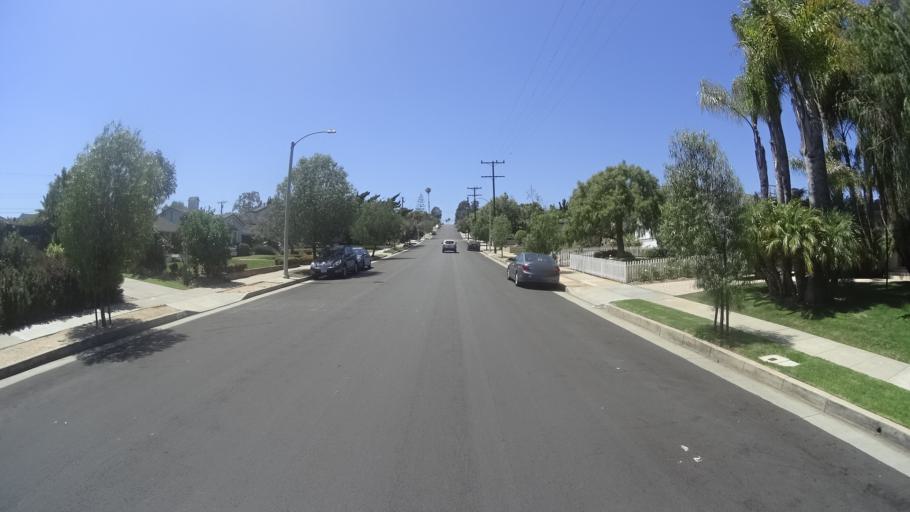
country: US
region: California
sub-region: Los Angeles County
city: Santa Monica
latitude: 34.0414
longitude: -118.4732
